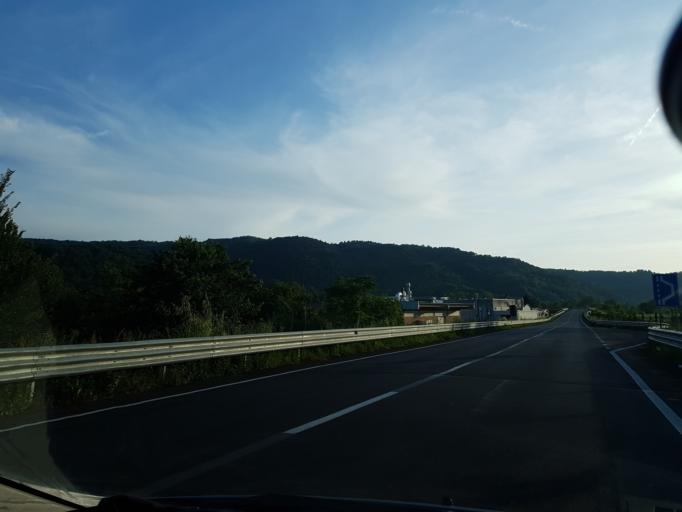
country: IT
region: Tuscany
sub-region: Provincia di Massa-Carrara
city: Fivizzano
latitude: 44.2027
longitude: 10.0925
